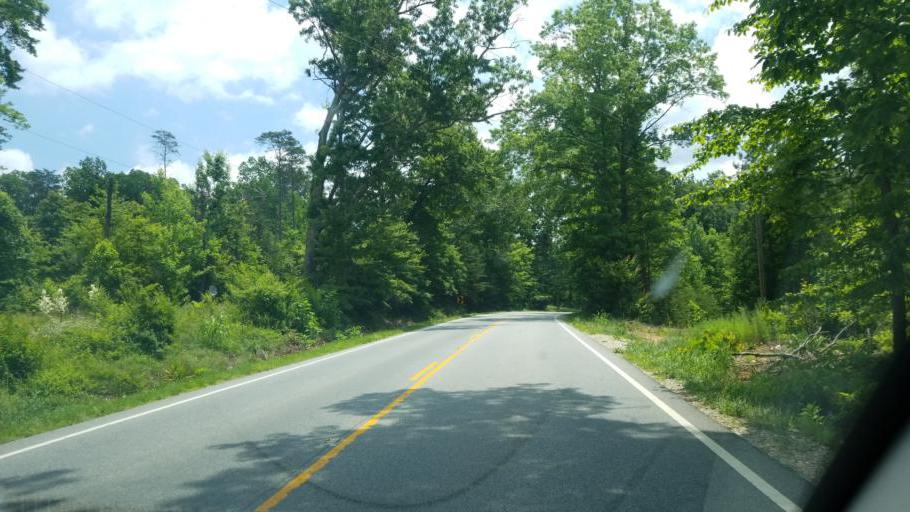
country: US
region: Virginia
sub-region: Nelson County
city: Lovingston
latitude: 37.5667
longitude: -78.8487
